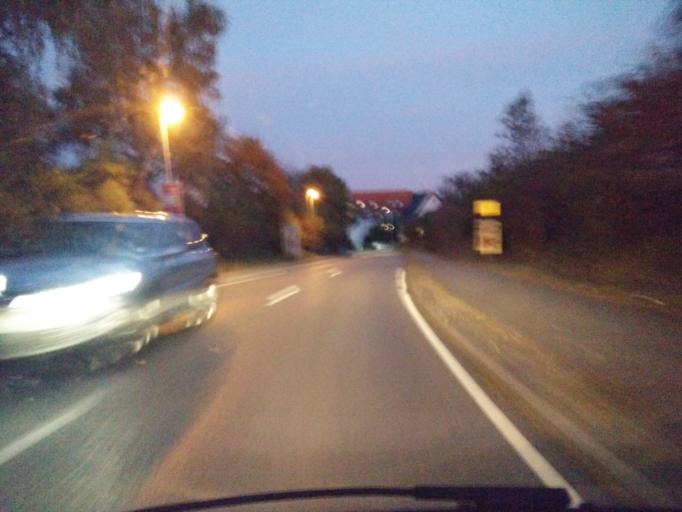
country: DE
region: Baden-Wuerttemberg
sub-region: Regierungsbezirk Stuttgart
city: Rutesheim
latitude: 48.8129
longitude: 8.9740
